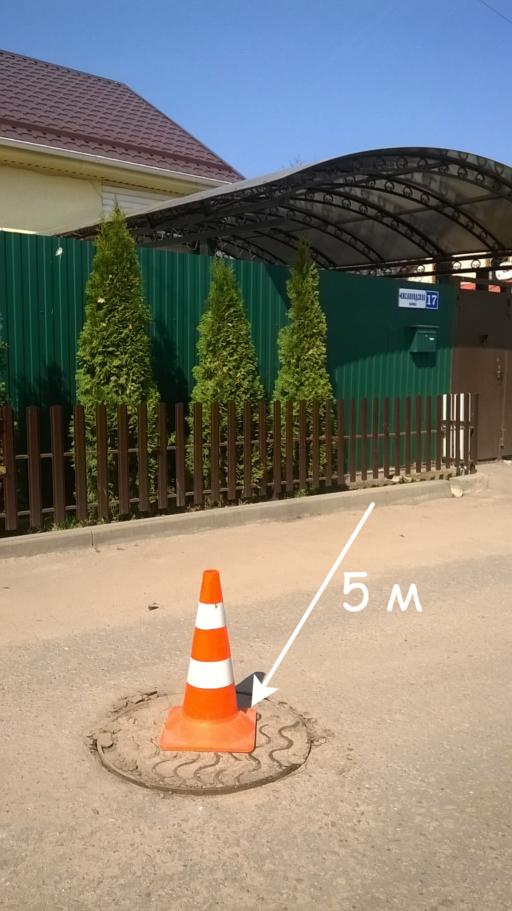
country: RU
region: Voronezj
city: Voronezh
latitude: 51.7041
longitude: 39.2357
